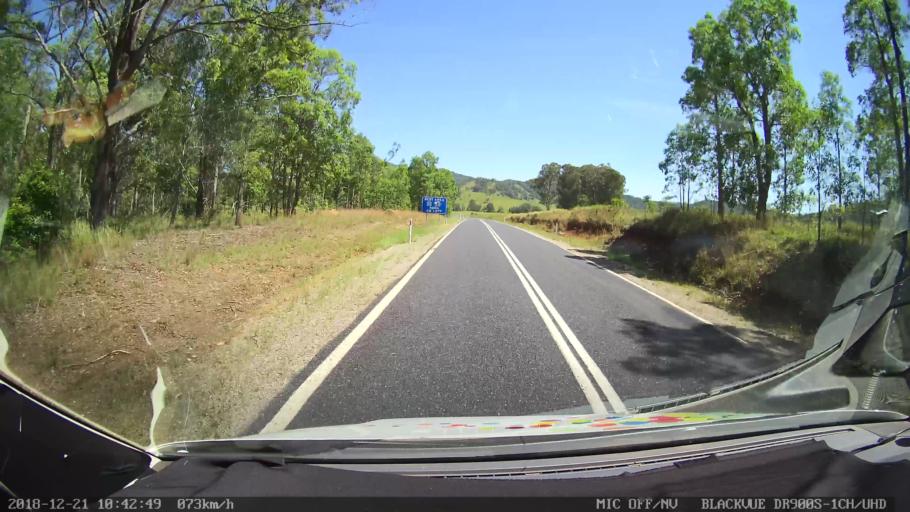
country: AU
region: New South Wales
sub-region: Clarence Valley
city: Gordon
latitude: -29.5813
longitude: 152.5607
